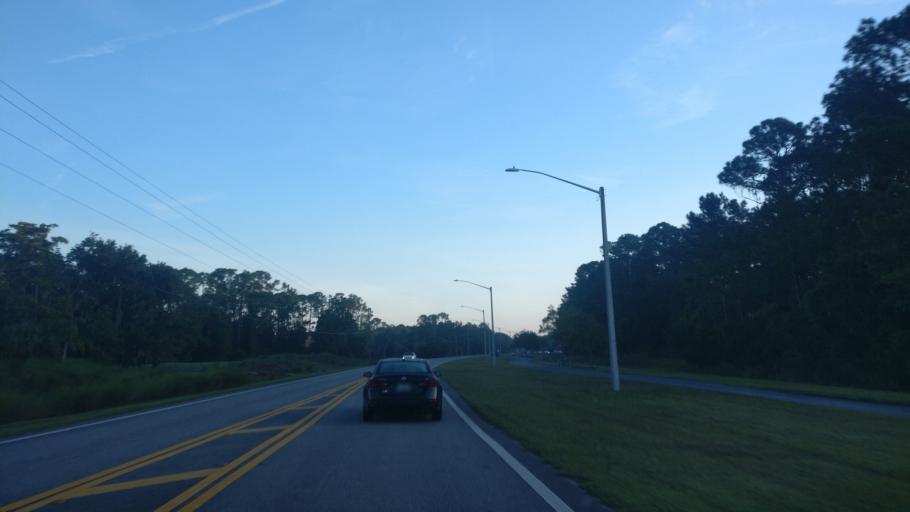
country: US
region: Florida
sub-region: Flagler County
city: Palm Coast
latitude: 29.5413
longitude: -81.2372
